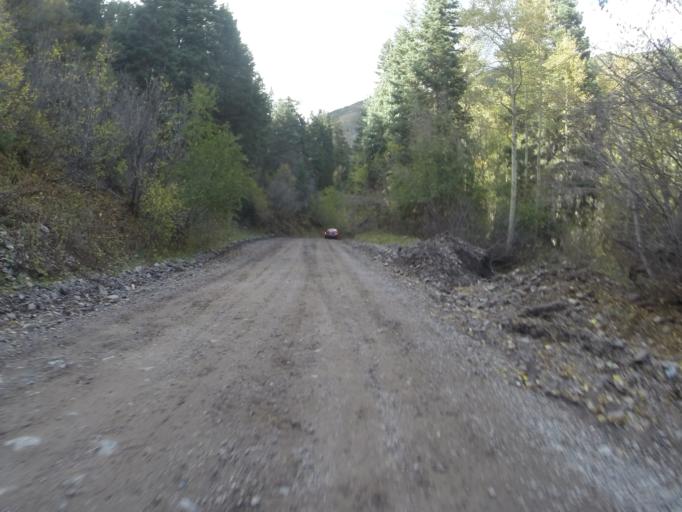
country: US
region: Utah
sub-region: Tooele County
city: Tooele
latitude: 40.4807
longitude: -112.1860
